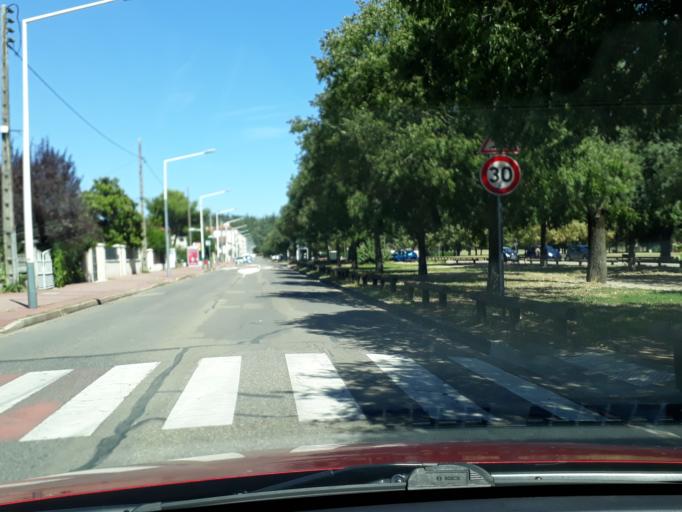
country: FR
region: Rhone-Alpes
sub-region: Departement du Rhone
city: Venissieux
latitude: 45.7181
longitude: 4.8922
